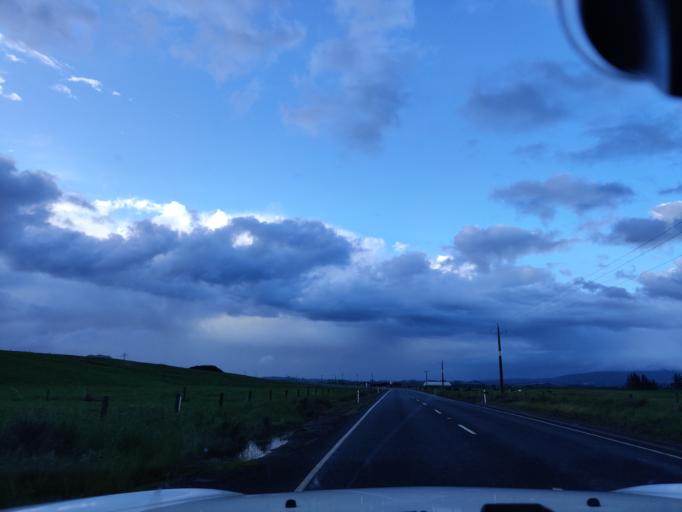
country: NZ
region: Waikato
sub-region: South Waikato District
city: Tokoroa
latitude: -38.3888
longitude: 175.7809
